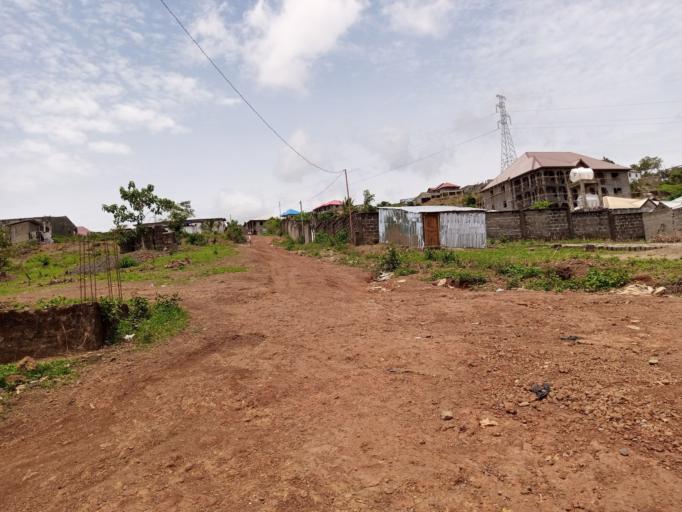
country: SL
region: Western Area
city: Hastings
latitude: 8.3816
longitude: -13.1452
